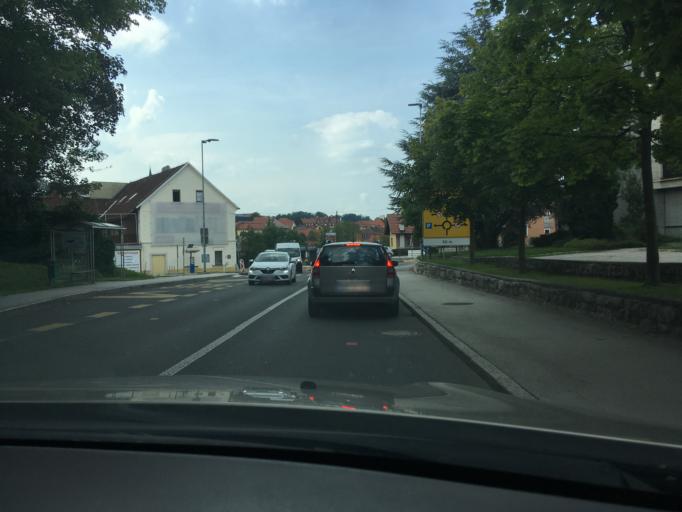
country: SI
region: Novo Mesto
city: Novo Mesto
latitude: 45.8006
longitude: 15.1724
